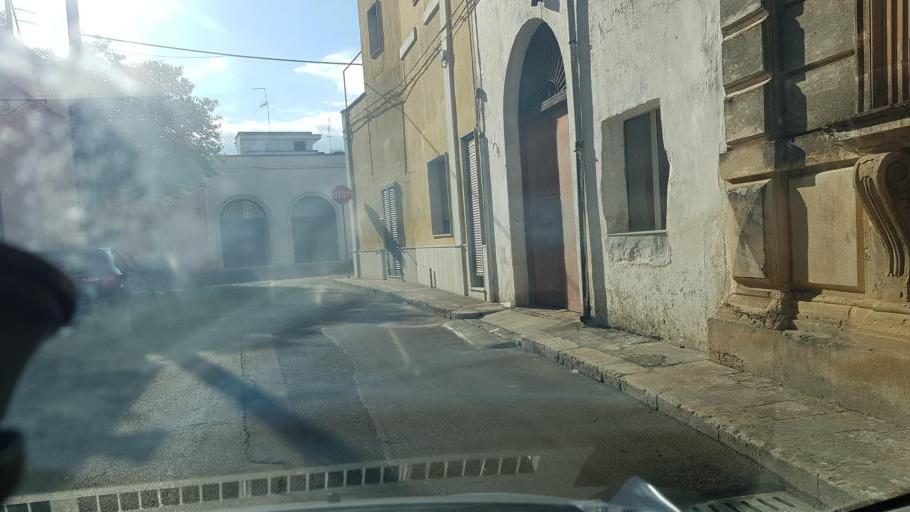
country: IT
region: Apulia
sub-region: Provincia di Lecce
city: Campi Salentina
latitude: 40.4010
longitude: 18.0177
